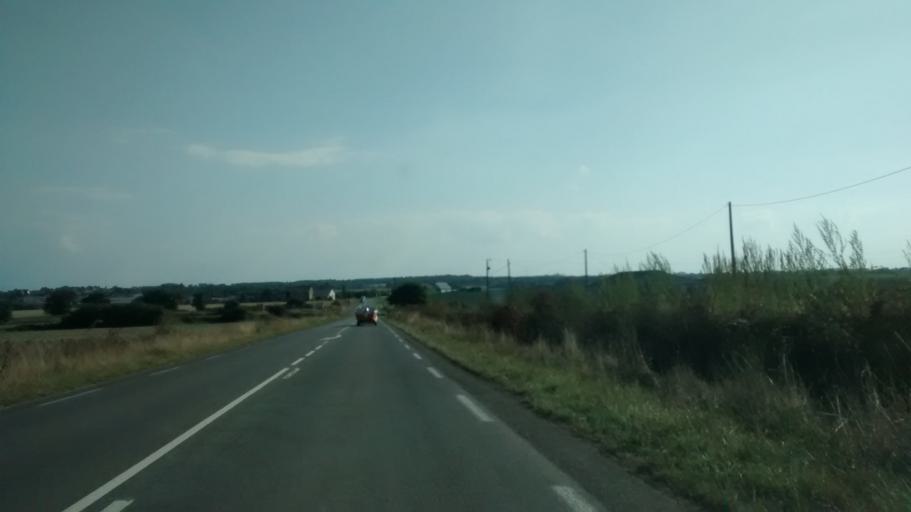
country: FR
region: Brittany
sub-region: Departement d'Ille-et-Vilaine
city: Saint-Meloir-des-Ondes
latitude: 48.6225
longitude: -1.9049
